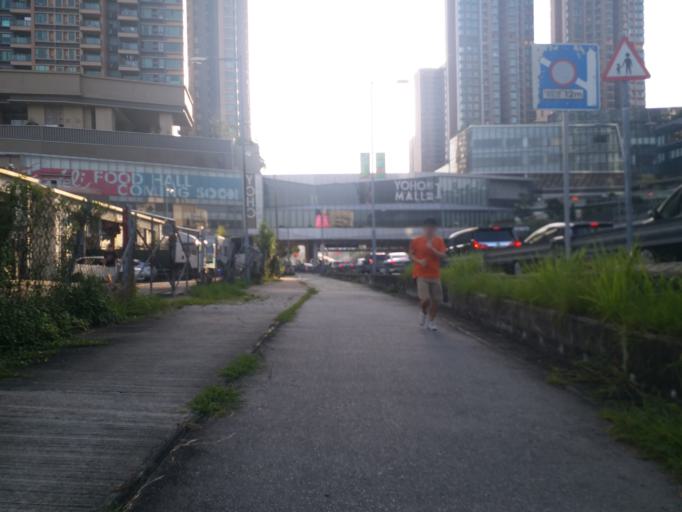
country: HK
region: Yuen Long
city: Yuen Long Kau Hui
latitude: 22.4442
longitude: 114.0385
